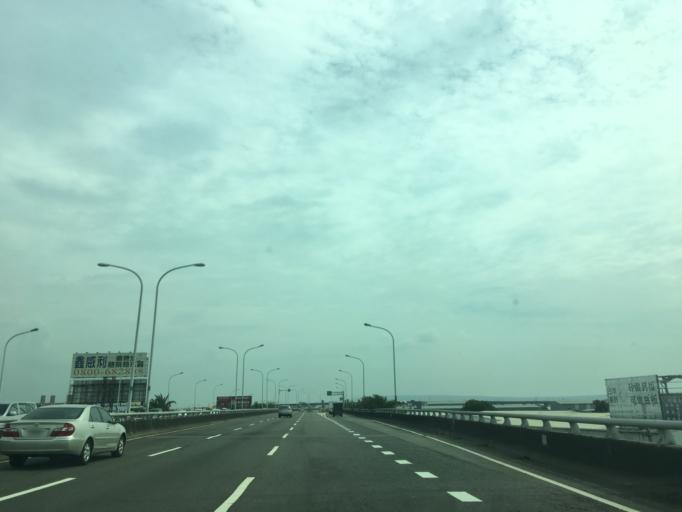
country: TW
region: Taiwan
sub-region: Taichung City
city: Taichung
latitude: 24.0774
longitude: 120.6640
